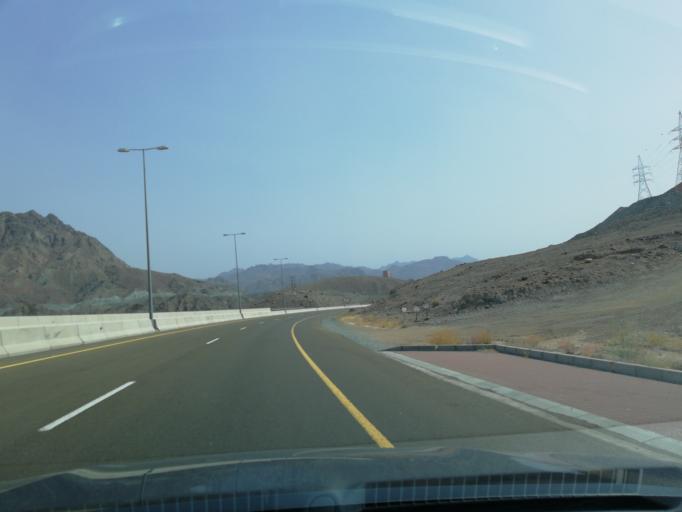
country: OM
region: Al Batinah
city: Al Liwa'
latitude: 24.2465
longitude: 56.3541
